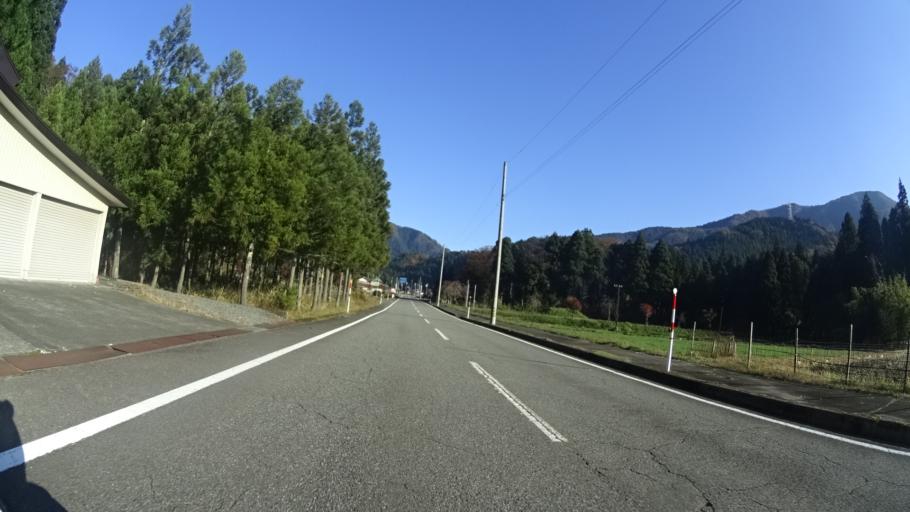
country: JP
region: Fukui
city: Maruoka
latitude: 36.1579
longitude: 136.3322
